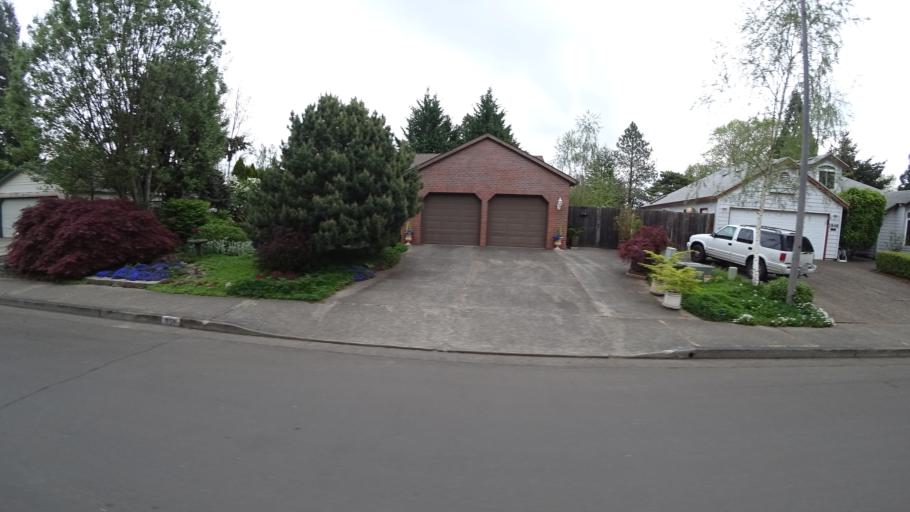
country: US
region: Oregon
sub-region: Washington County
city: Hillsboro
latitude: 45.5393
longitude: -122.9862
